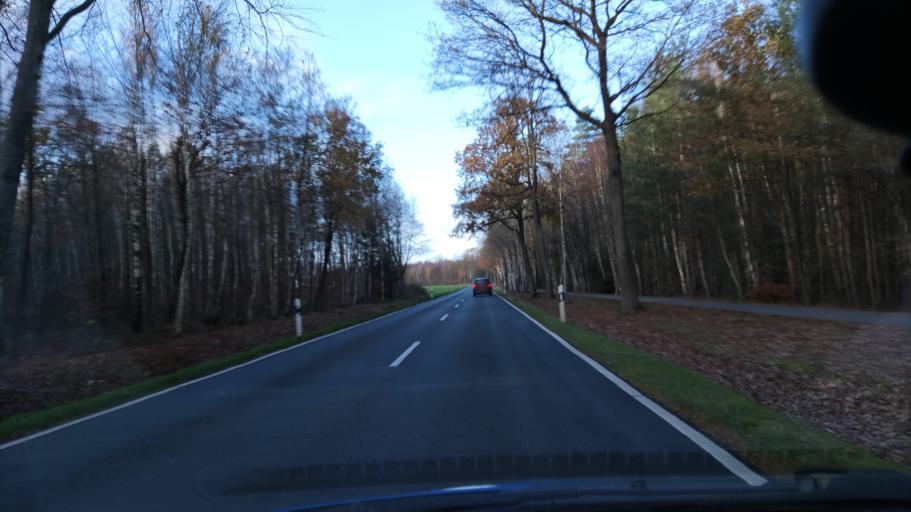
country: DE
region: Lower Saxony
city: Soltau
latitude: 53.0517
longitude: 9.8238
